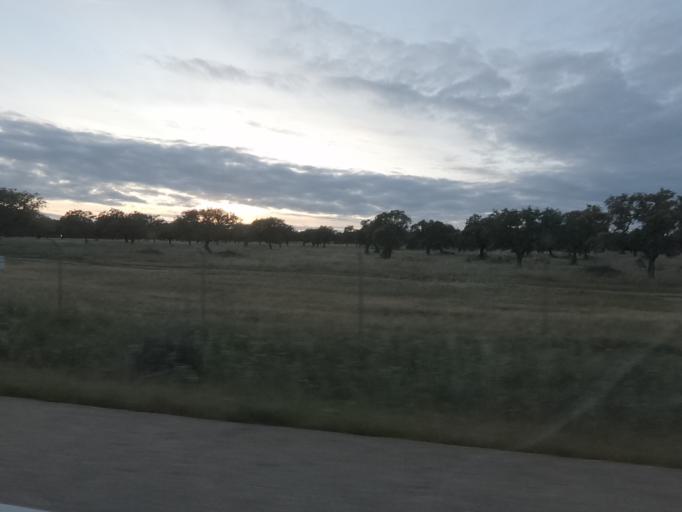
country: ES
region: Extremadura
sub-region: Provincia de Badajoz
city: Villar del Rey
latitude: 39.0027
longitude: -6.8636
